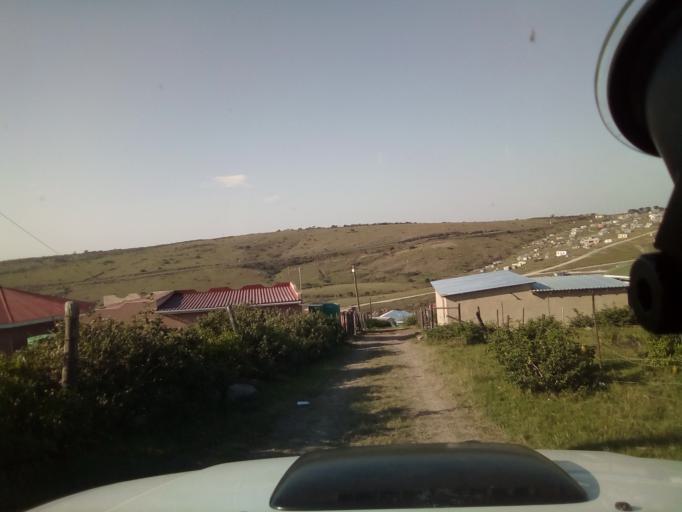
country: ZA
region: Eastern Cape
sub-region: Buffalo City Metropolitan Municipality
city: East London
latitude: -32.8465
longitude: 27.9893
